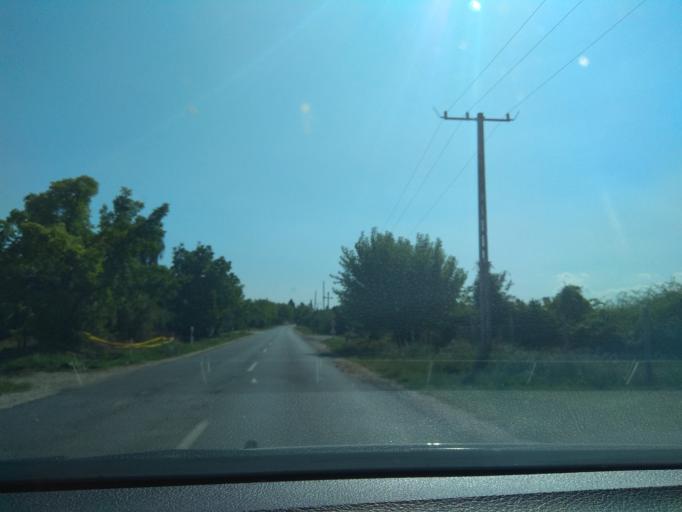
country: HU
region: Borsod-Abauj-Zemplen
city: Malyi
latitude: 48.0357
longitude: 20.7736
